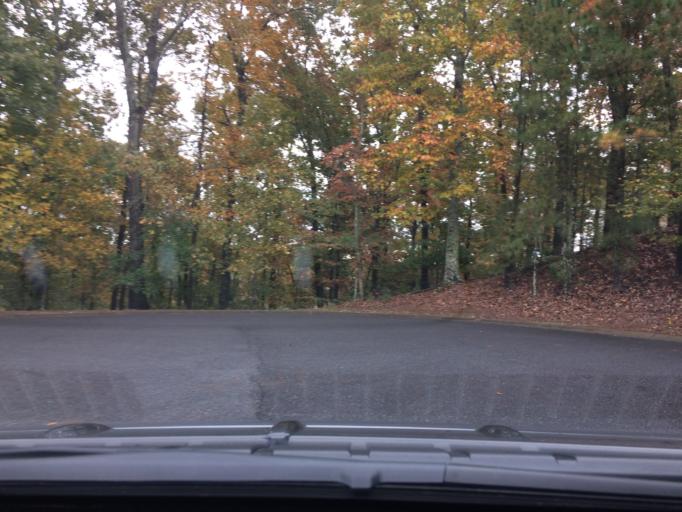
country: US
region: Georgia
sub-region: Fulton County
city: Johns Creek
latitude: 34.0053
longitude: -84.2478
